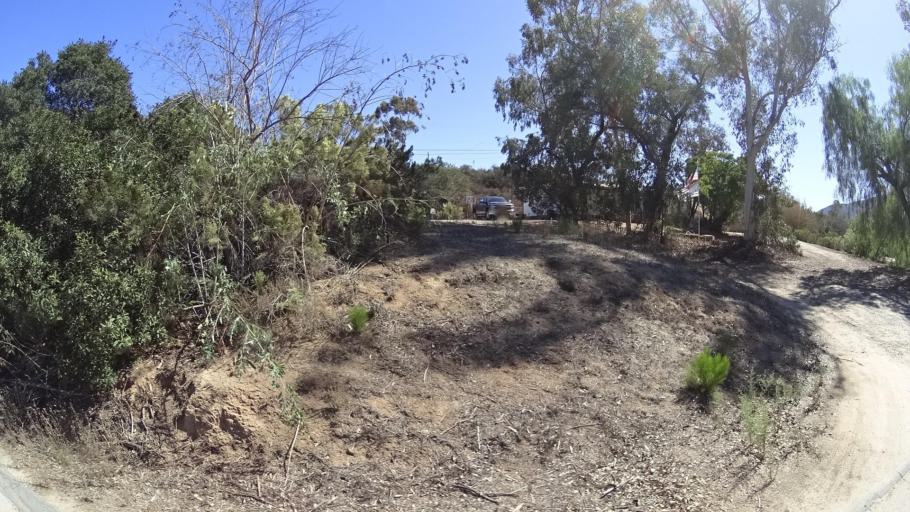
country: US
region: California
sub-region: San Diego County
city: Harbison Canyon
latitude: 32.7904
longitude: -116.8060
